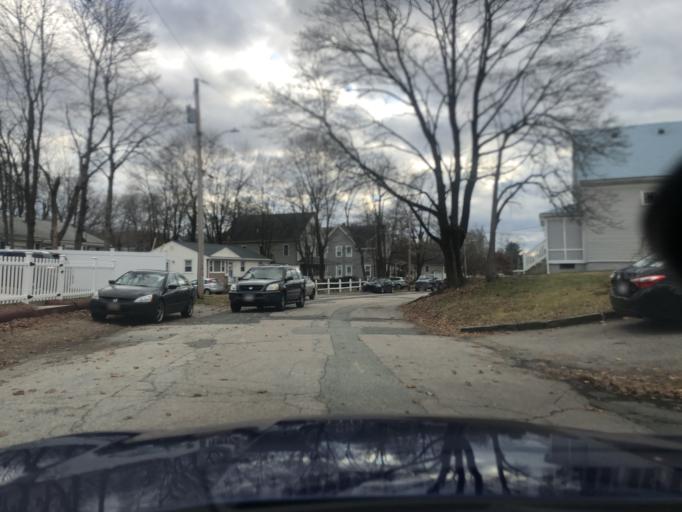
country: US
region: Massachusetts
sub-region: Plymouth County
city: Brockton
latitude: 42.1121
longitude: -71.0180
